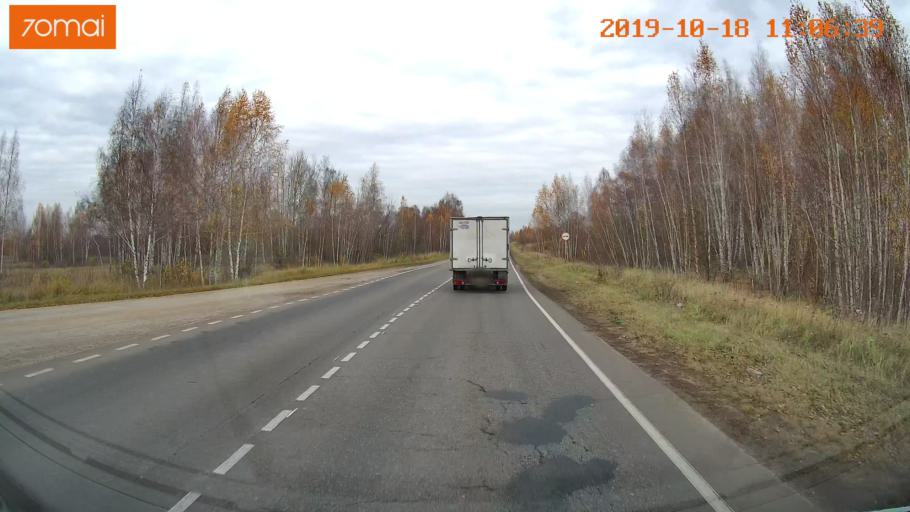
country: RU
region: Tula
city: Kimovsk
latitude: 53.9201
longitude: 38.5349
